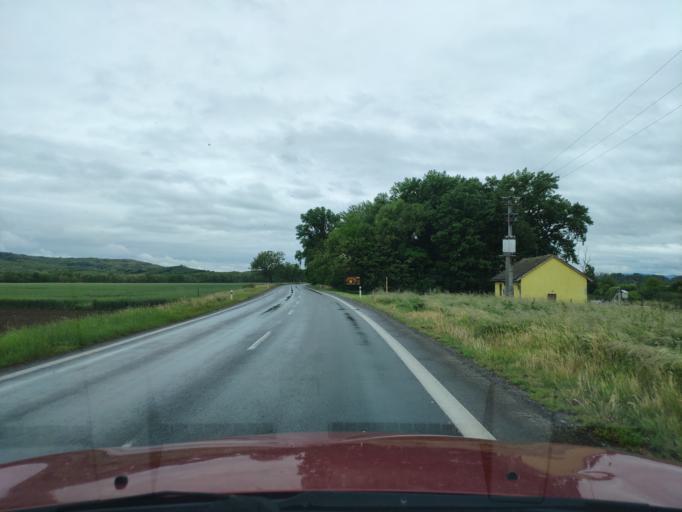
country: HU
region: Borsod-Abauj-Zemplen
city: Karcsa
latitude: 48.3939
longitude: 21.7997
